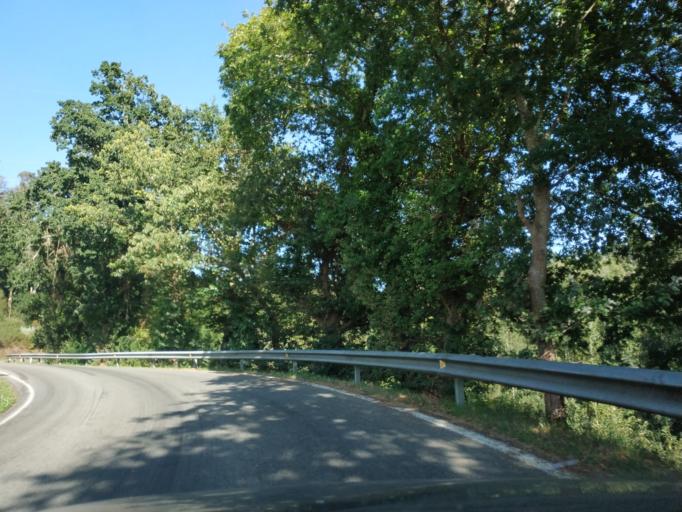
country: ES
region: Galicia
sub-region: Provincia da Coruna
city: Cerceda
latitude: 43.2330
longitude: -8.4759
